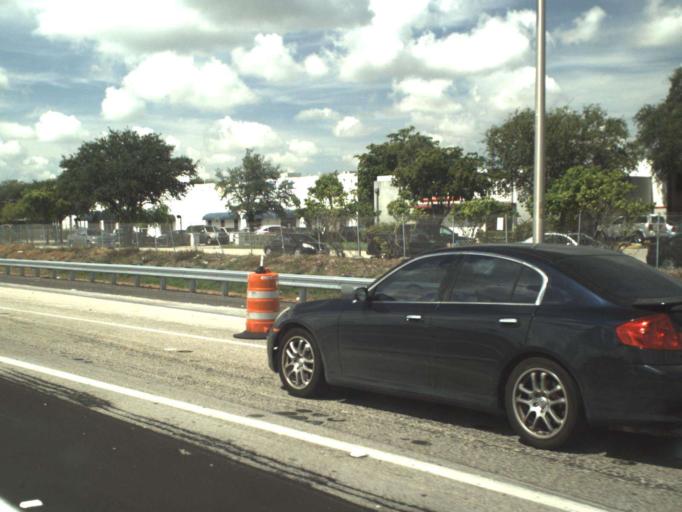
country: US
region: Florida
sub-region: Broward County
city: Dania Beach
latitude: 26.0438
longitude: -80.1631
